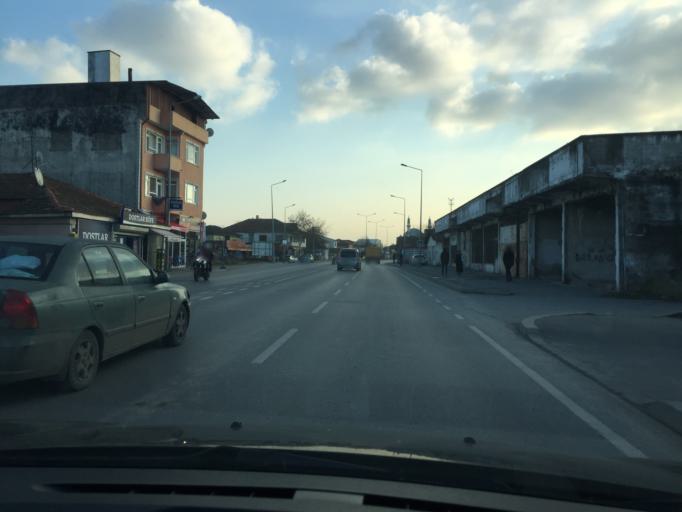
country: TR
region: Sakarya
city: Adapazari
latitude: 40.7926
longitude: 30.4072
